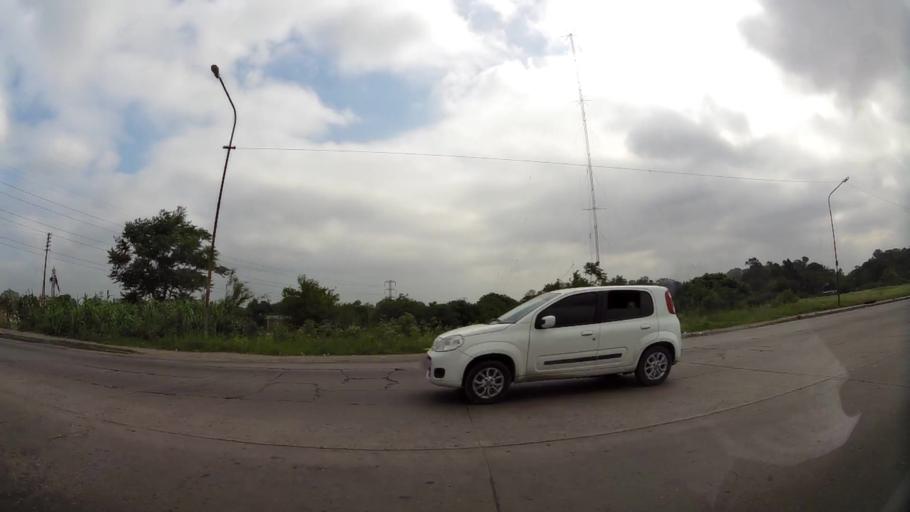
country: AR
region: Buenos Aires
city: San Justo
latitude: -34.7237
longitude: -58.5341
